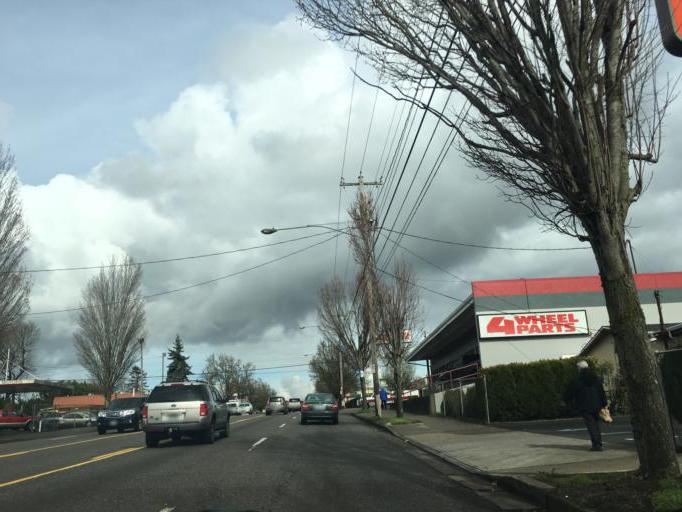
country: US
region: Oregon
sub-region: Multnomah County
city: Lents
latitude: 45.5027
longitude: -122.5786
